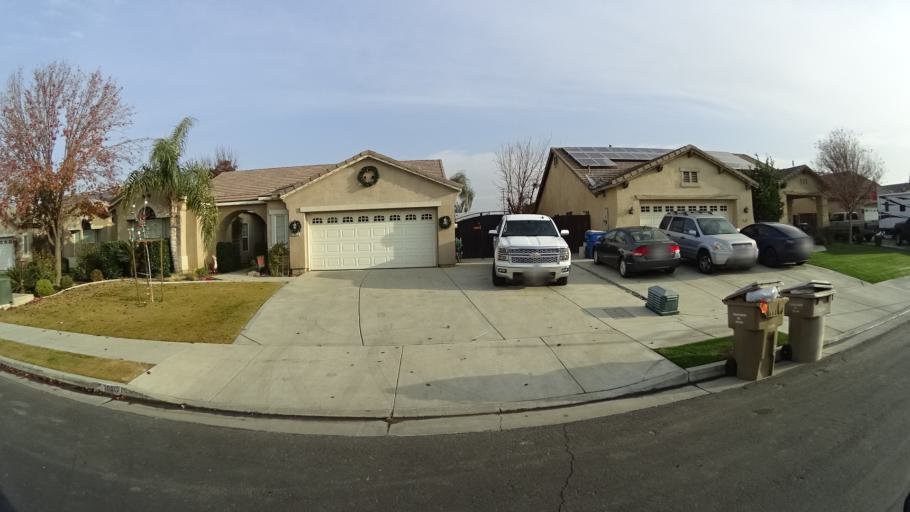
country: US
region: California
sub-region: Kern County
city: Greenacres
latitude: 35.4258
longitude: -119.1234
